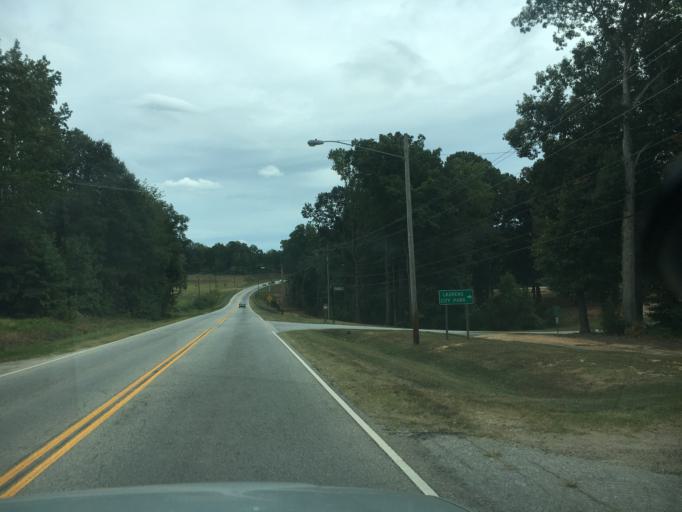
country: US
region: South Carolina
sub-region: Laurens County
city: Watts Mills
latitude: 34.5018
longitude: -81.9918
